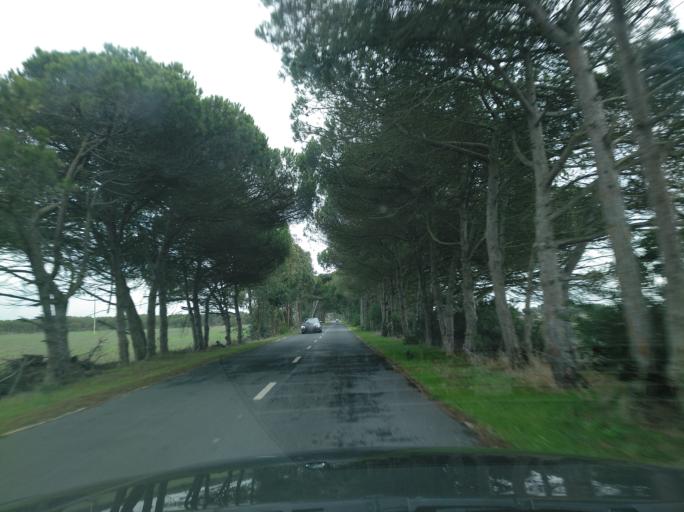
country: PT
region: Beja
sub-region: Odemira
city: Vila Nova de Milfontes
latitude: 37.7094
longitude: -8.7758
